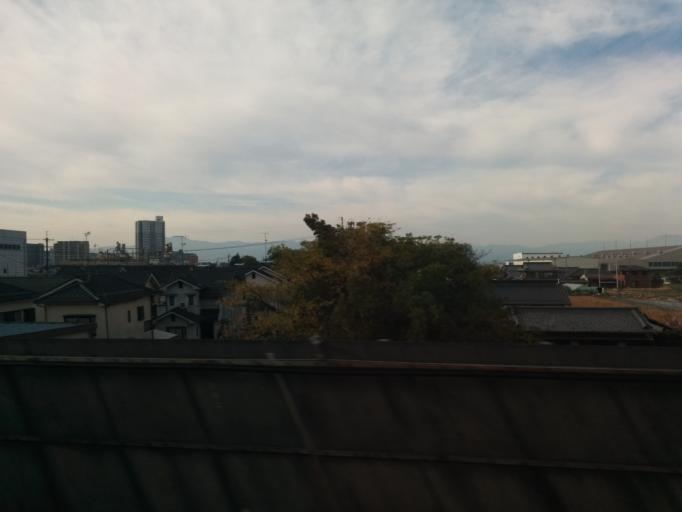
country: JP
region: Shiga Prefecture
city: Moriyama
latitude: 35.0350
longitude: 135.9954
